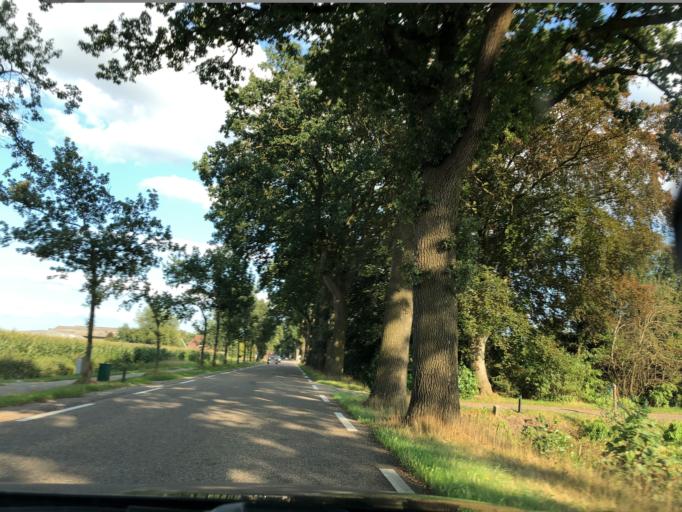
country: NL
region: Groningen
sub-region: Gemeente Vlagtwedde
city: Vlagtwedde
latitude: 53.0241
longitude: 7.1449
